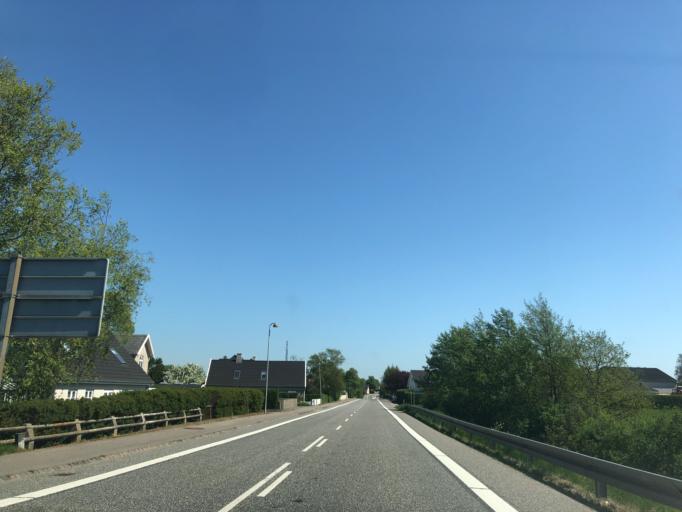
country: DK
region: Zealand
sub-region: Slagelse Kommune
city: Skaelskor
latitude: 55.3053
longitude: 11.2591
